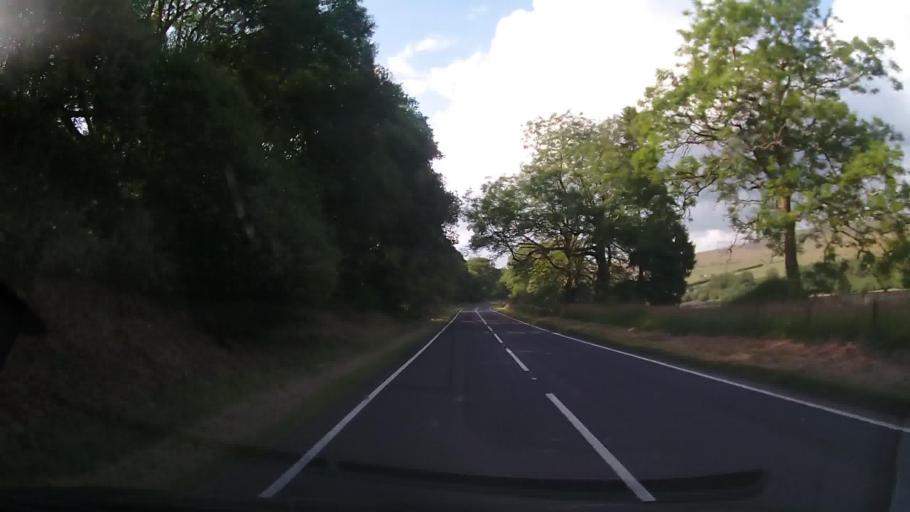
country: GB
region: Wales
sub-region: Gwynedd
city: Bala
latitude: 52.9543
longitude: -3.7202
